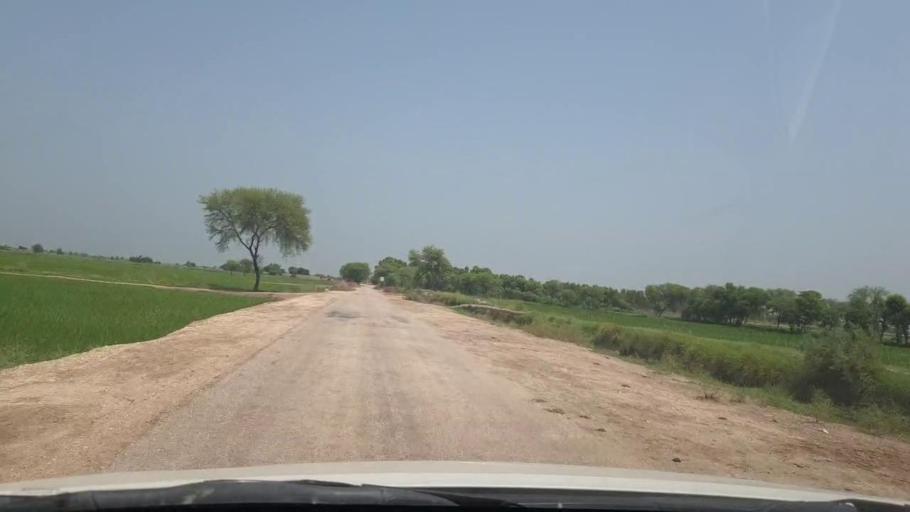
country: PK
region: Sindh
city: Rustam jo Goth
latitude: 28.0287
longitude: 68.7762
